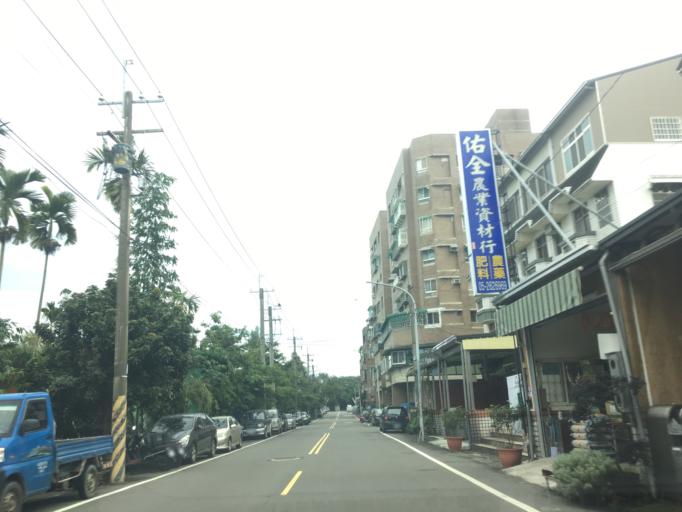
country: TW
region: Taiwan
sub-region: Yunlin
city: Douliu
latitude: 23.5885
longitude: 120.5499
